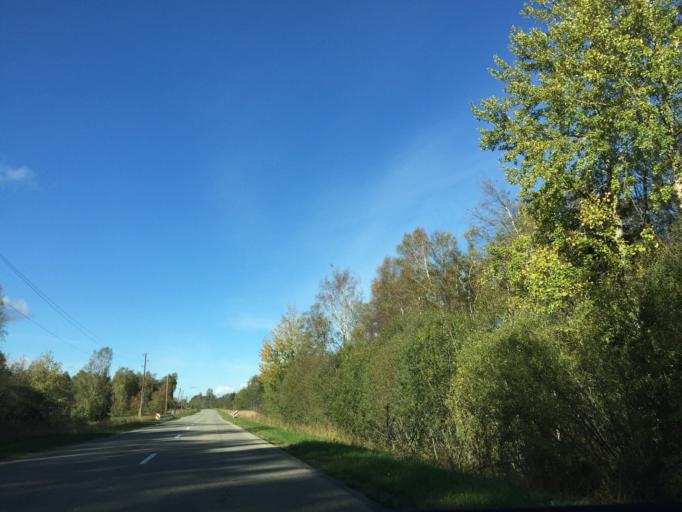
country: LV
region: Rojas
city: Roja
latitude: 57.4412
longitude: 22.9044
